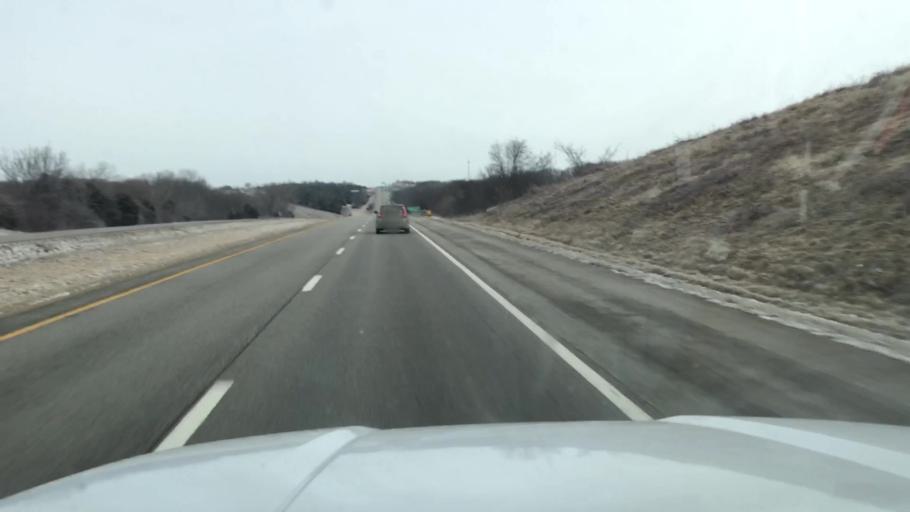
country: US
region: Missouri
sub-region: Andrew County
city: Country Club Village
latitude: 39.8790
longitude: -94.8444
